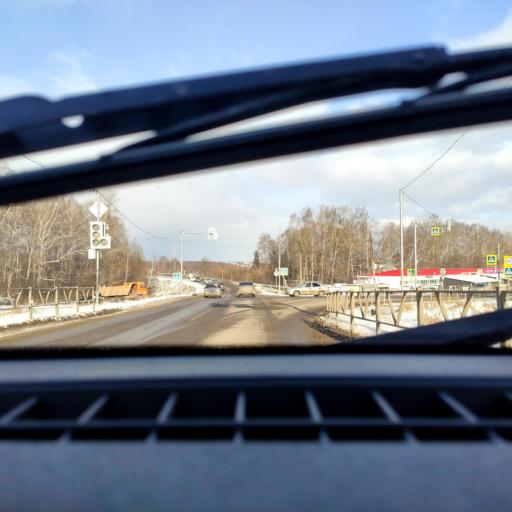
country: RU
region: Bashkortostan
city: Iglino
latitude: 54.8289
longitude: 56.4248
